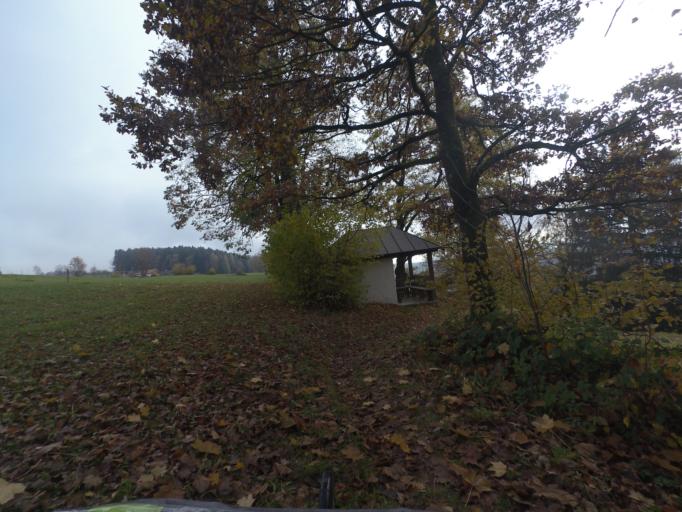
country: AT
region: Salzburg
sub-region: Politischer Bezirk Hallein
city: Adnet
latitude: 47.6717
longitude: 13.1364
